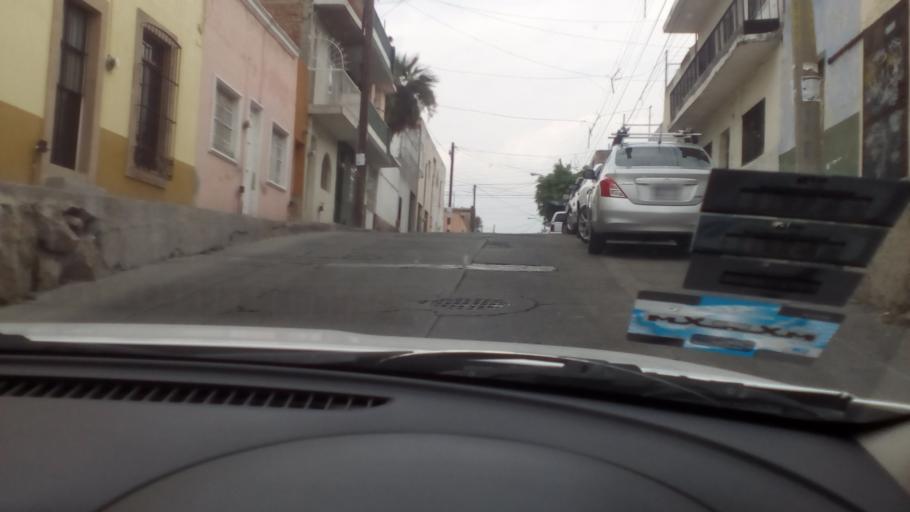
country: MX
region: Guanajuato
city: Leon
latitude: 21.1237
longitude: -101.6889
